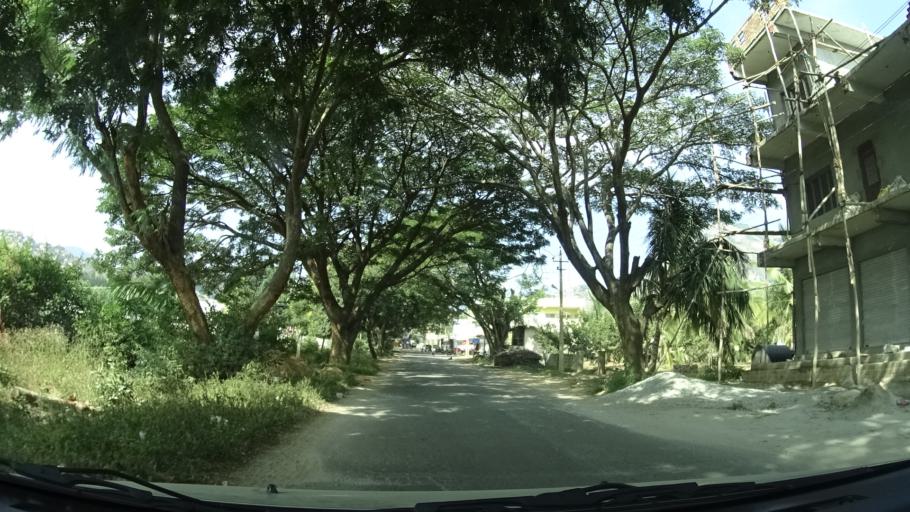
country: IN
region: Karnataka
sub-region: Chikkaballapur
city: Chik Ballapur
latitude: 13.4069
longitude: 77.6987
